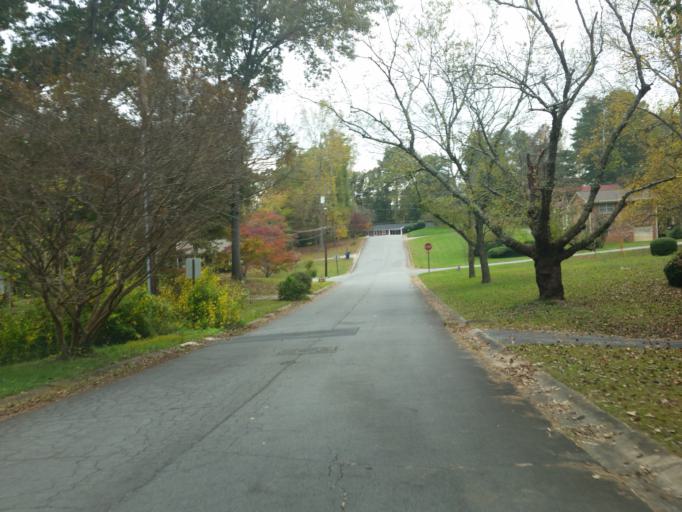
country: US
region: Georgia
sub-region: Cobb County
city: Marietta
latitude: 33.9599
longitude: -84.4711
